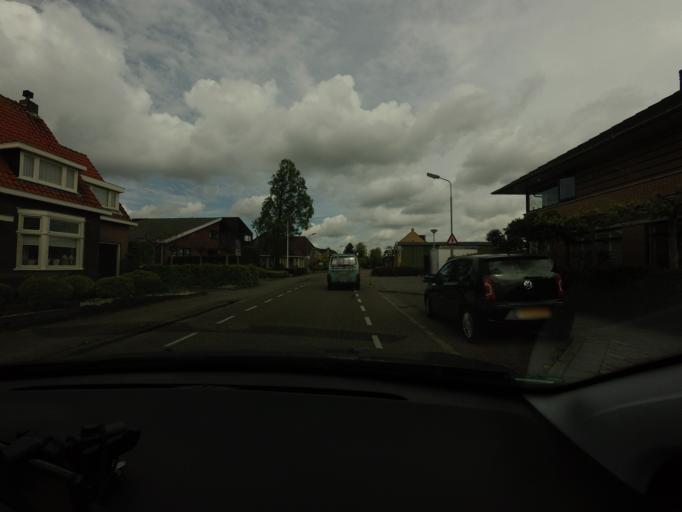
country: NL
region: North Holland
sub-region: Gemeente Landsmeer
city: Landsmeer
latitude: 52.4466
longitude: 4.8722
